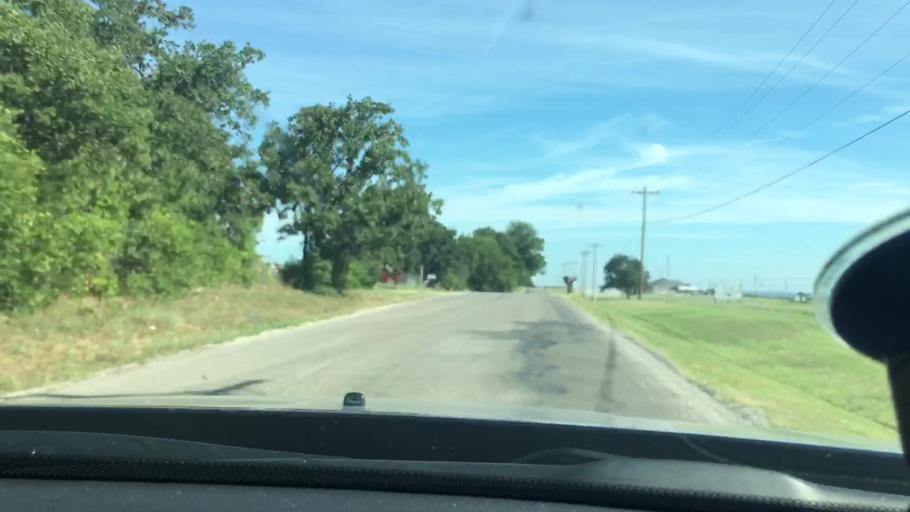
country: US
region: Oklahoma
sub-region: Carter County
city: Lone Grove
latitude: 34.2219
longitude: -97.2474
